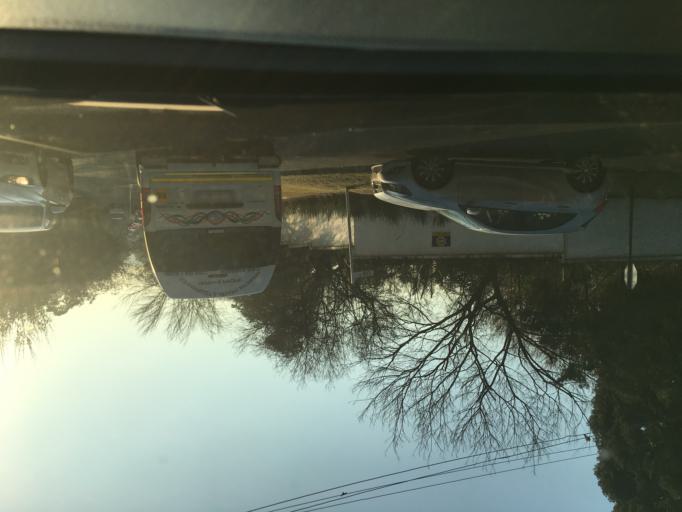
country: ZA
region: Gauteng
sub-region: City of Johannesburg Metropolitan Municipality
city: Diepsloot
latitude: -26.0709
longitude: 27.9999
